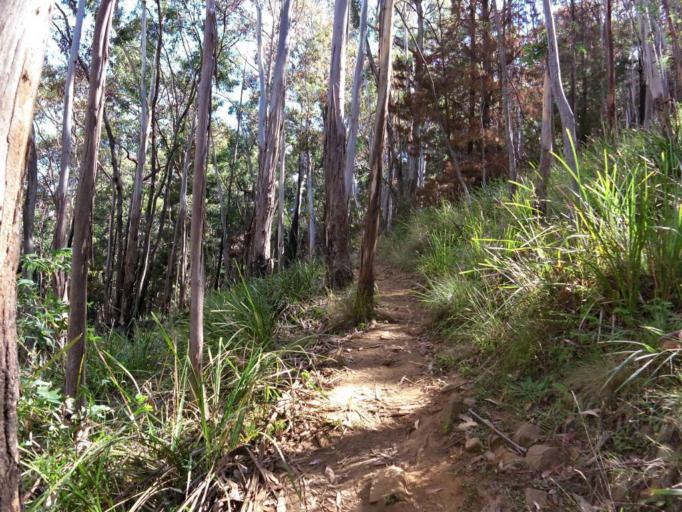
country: AU
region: Victoria
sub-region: Hume
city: Sunbury
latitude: -37.3950
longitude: 144.5727
